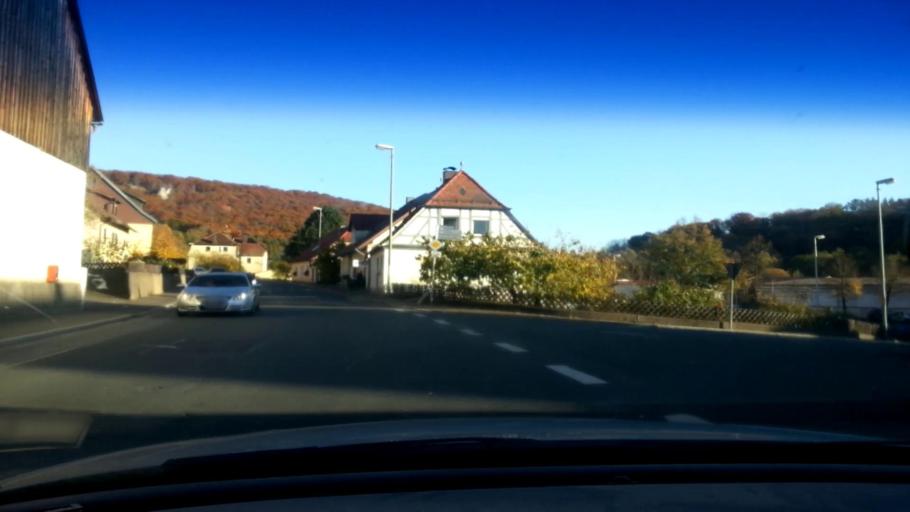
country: DE
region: Bavaria
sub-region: Upper Franconia
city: Heiligenstadt
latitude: 49.8636
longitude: 11.1718
